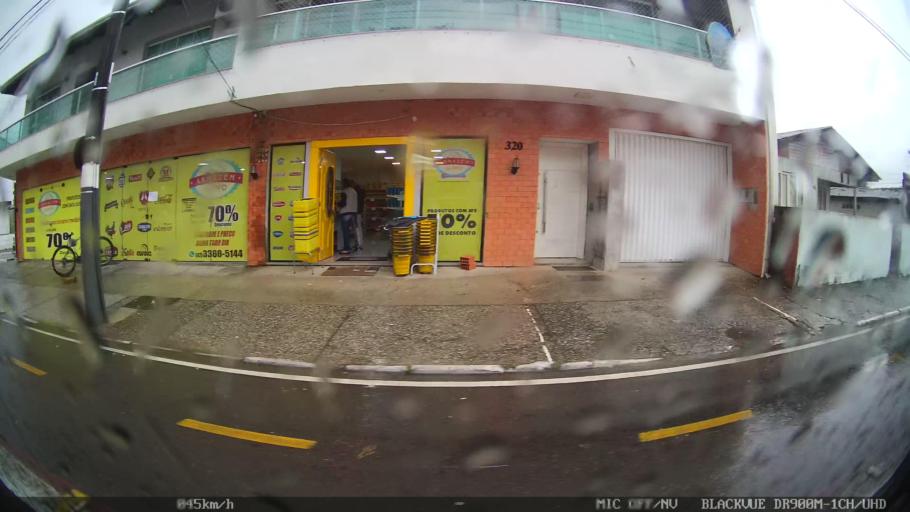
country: BR
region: Santa Catarina
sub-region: Balneario Camboriu
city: Balneario Camboriu
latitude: -27.0077
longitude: -48.6288
